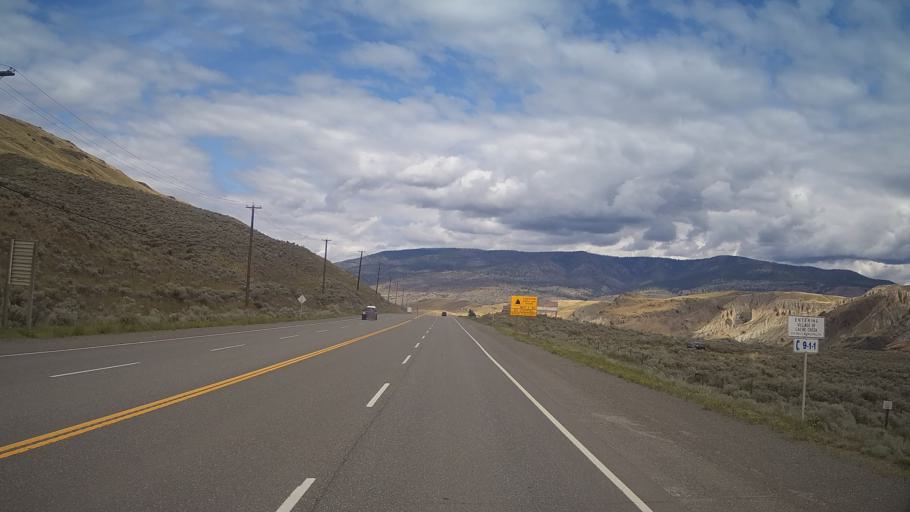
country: CA
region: British Columbia
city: Cache Creek
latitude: 50.7756
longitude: -121.3128
